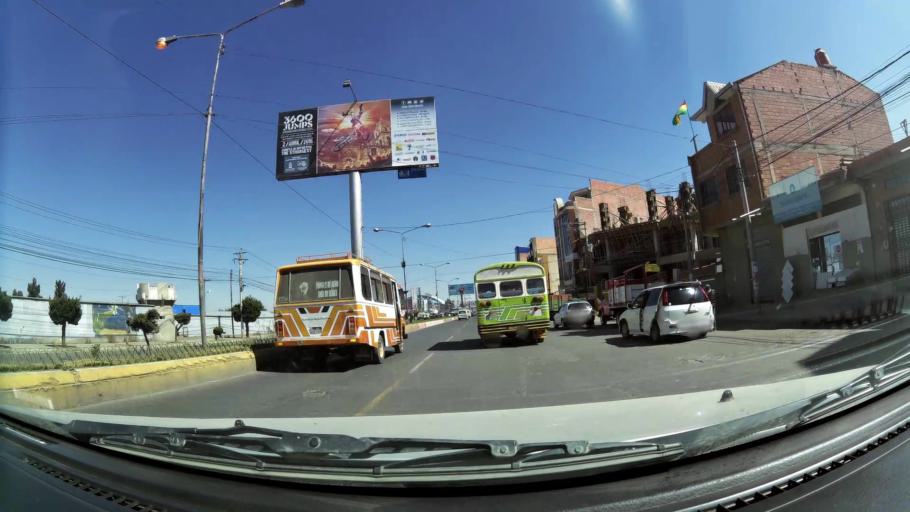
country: BO
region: La Paz
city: La Paz
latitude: -16.5003
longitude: -68.1731
